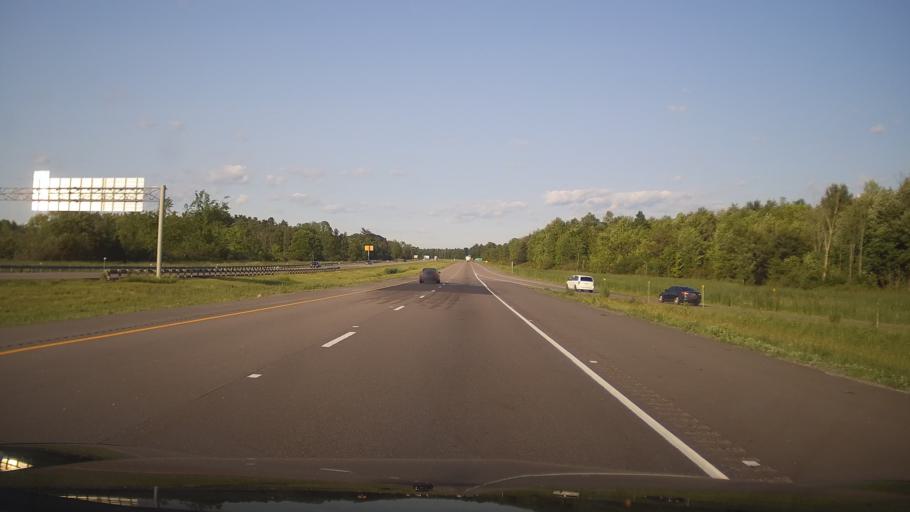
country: US
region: New York
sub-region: Jefferson County
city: Alexandria Bay
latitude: 44.3825
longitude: -75.9803
